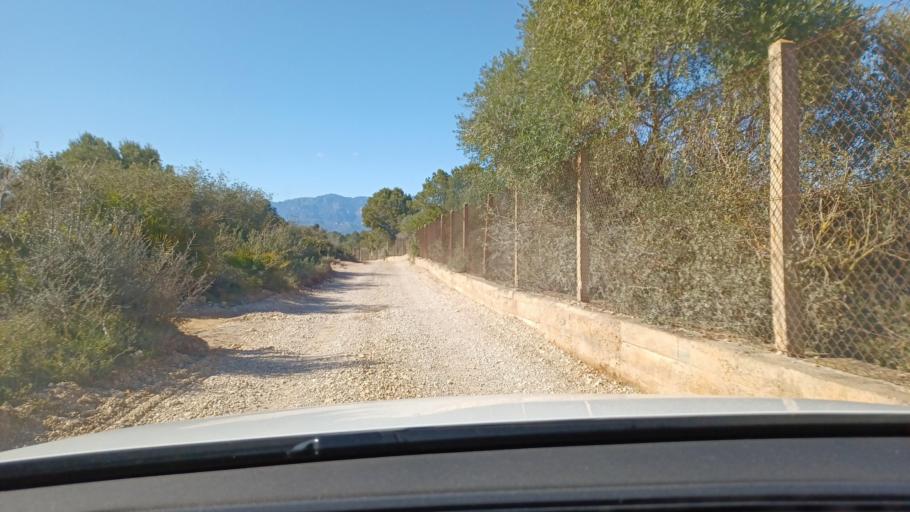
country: ES
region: Catalonia
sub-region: Provincia de Tarragona
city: Masdenverge
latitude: 40.6855
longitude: 0.5371
